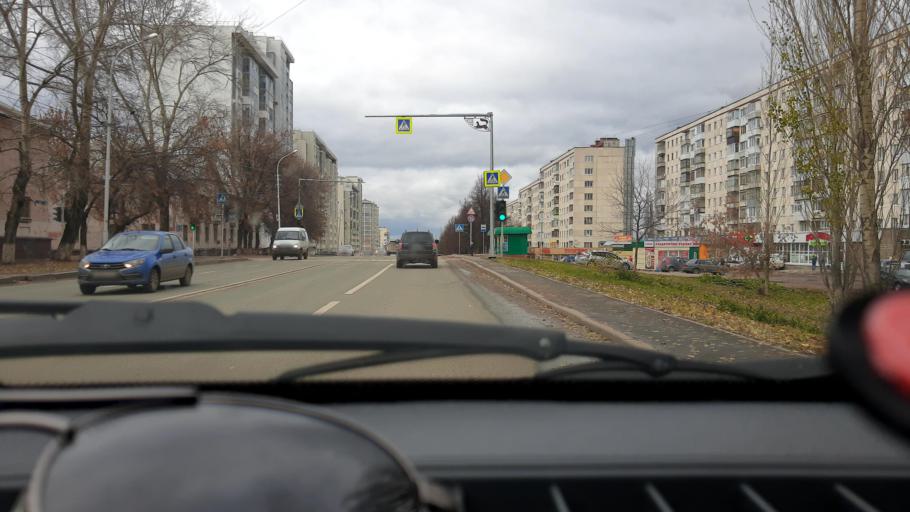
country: RU
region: Bashkortostan
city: Ufa
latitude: 54.7870
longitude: 56.0399
